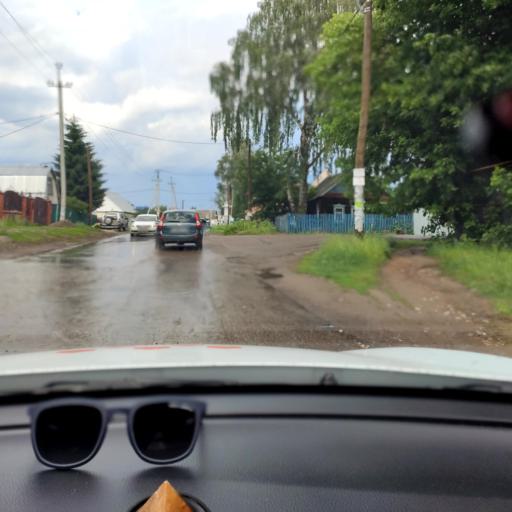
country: RU
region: Tatarstan
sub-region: Zelenodol'skiy Rayon
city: Vasil'yevo
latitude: 55.8296
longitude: 48.7077
